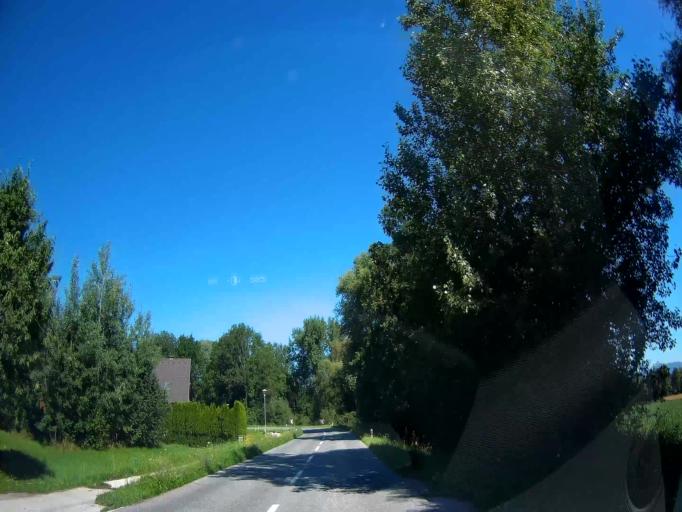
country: AT
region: Carinthia
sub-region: Politischer Bezirk Klagenfurt Land
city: Ebenthal
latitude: 46.6054
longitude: 14.4063
